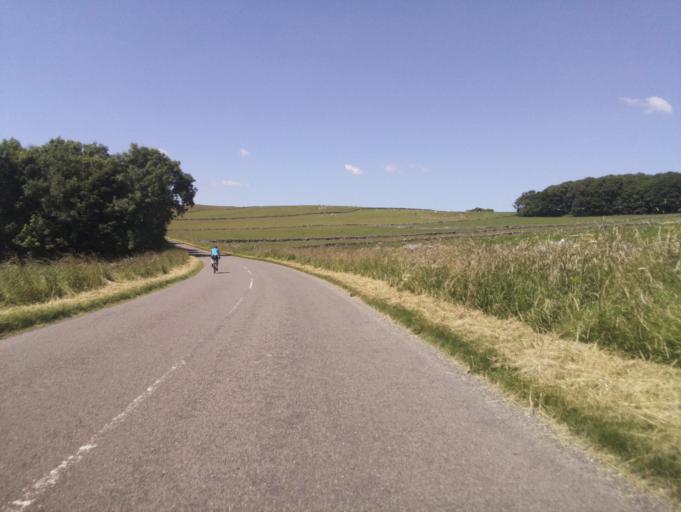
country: GB
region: England
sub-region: Derbyshire
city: Tideswell
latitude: 53.2756
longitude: -1.8342
